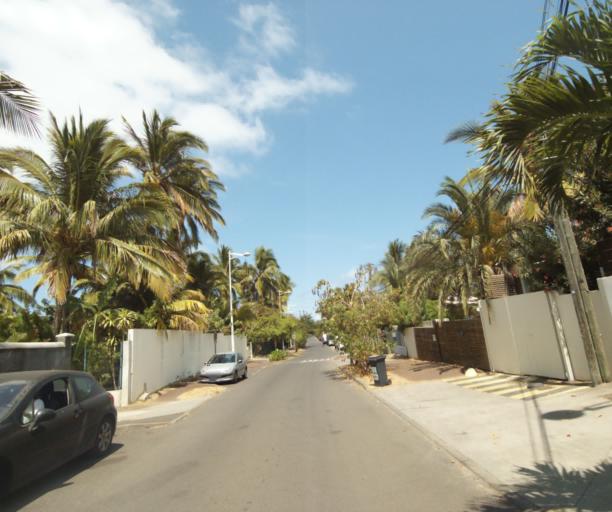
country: RE
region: Reunion
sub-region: Reunion
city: Trois-Bassins
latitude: -21.0921
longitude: 55.2378
